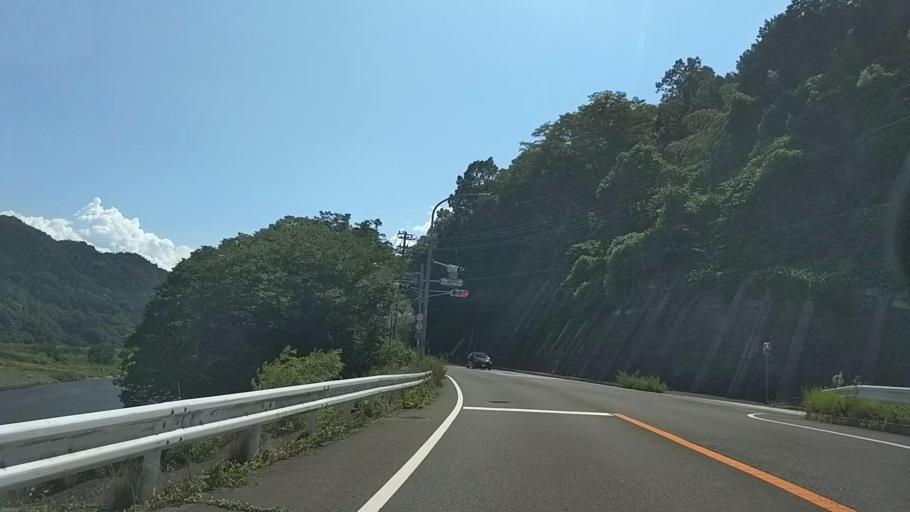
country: JP
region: Yamanashi
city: Ryuo
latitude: 35.4815
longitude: 138.4472
